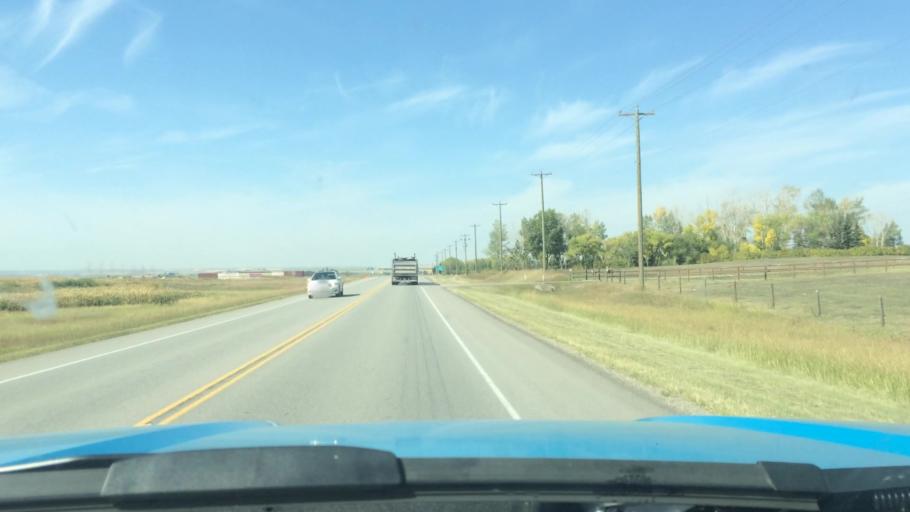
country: CA
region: Alberta
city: Airdrie
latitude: 51.2126
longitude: -113.9707
